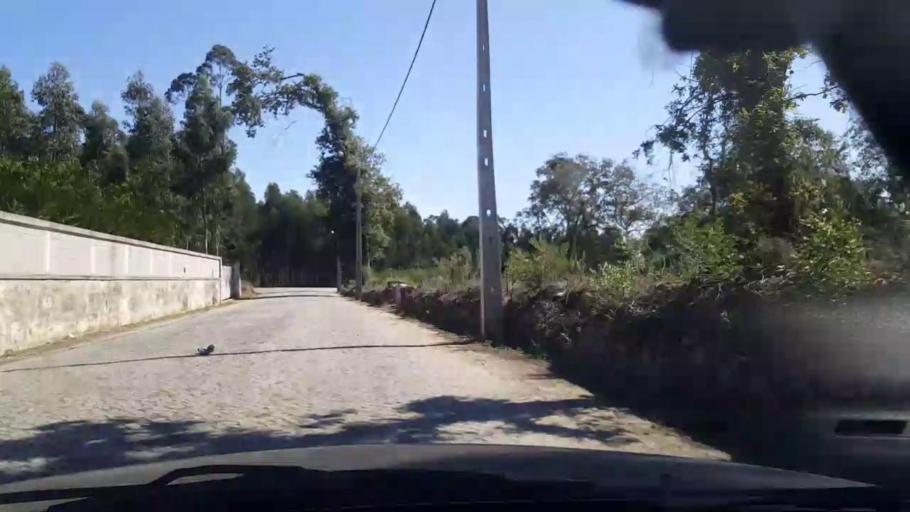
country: PT
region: Porto
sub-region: Vila do Conde
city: Arvore
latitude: 41.3123
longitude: -8.6862
